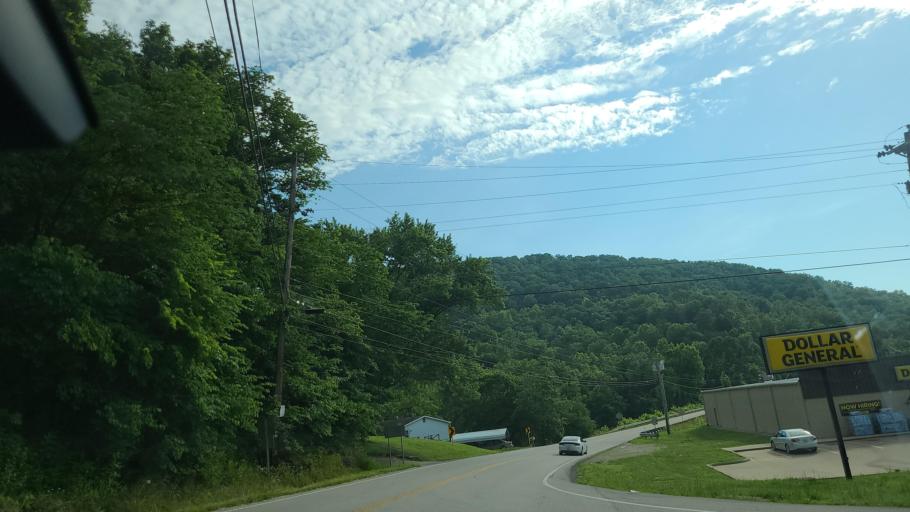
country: US
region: Kentucky
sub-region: Whitley County
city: Williamsburg
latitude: 36.7421
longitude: -84.1047
